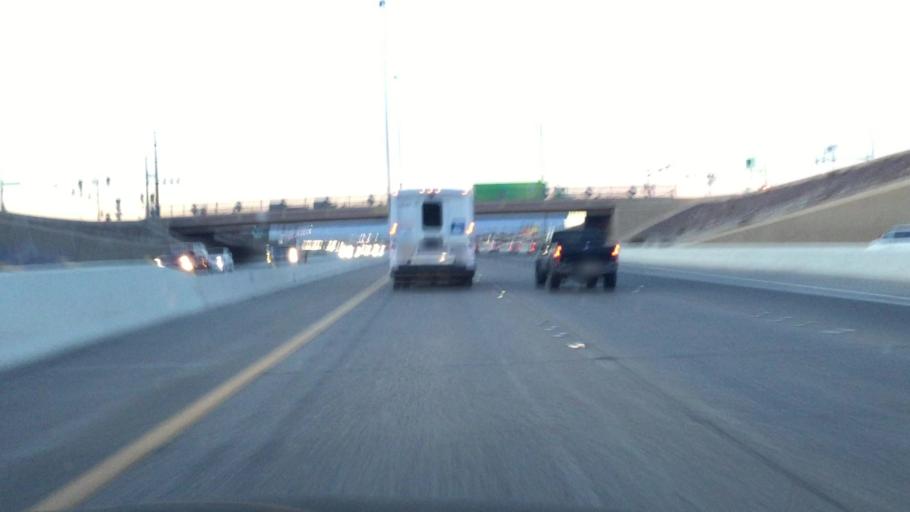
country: US
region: Nevada
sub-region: Clark County
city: Henderson
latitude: 36.0449
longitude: -115.0221
